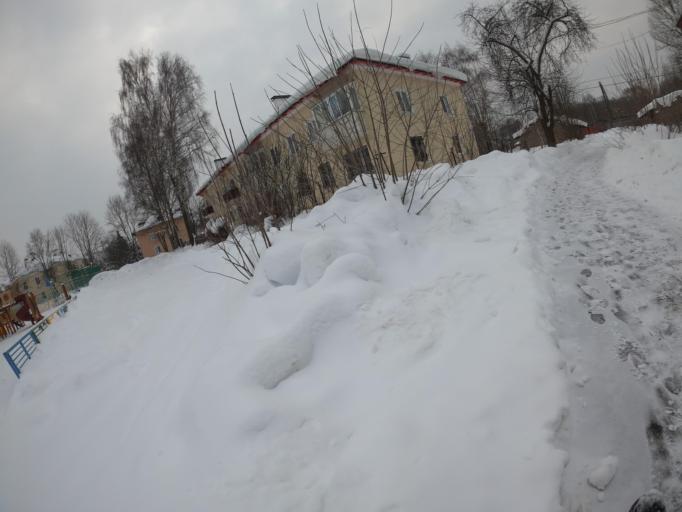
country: RU
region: Moskovskaya
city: Elektrogorsk
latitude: 55.8823
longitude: 38.7892
